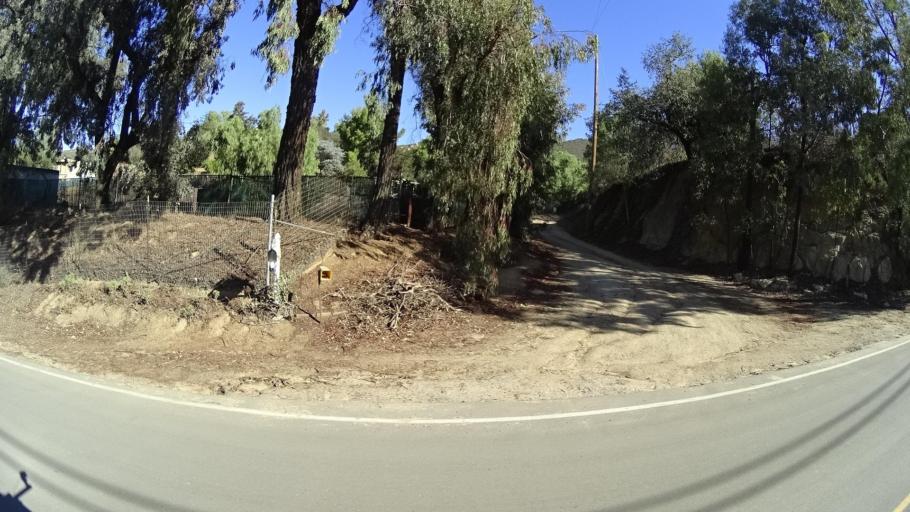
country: MX
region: Baja California
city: Tecate
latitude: 32.6754
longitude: -116.7163
